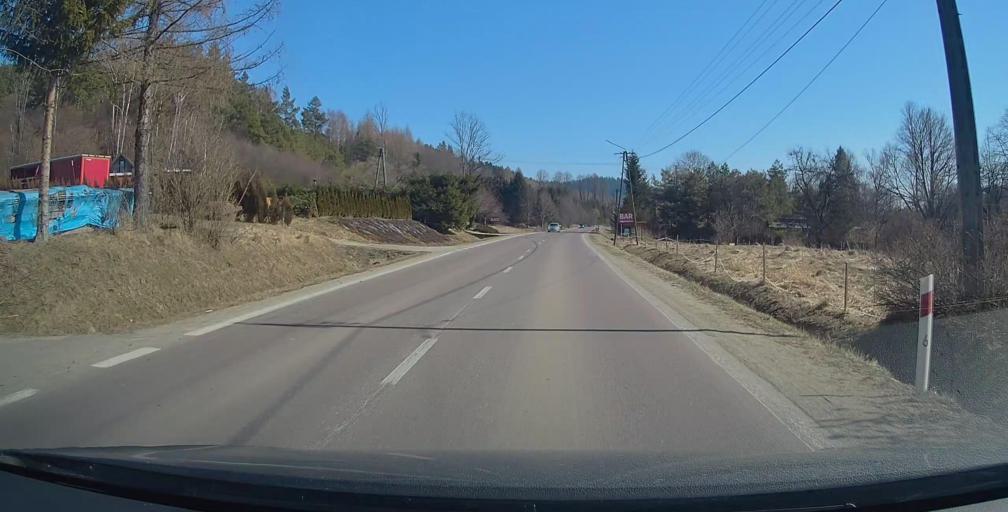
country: PL
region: Subcarpathian Voivodeship
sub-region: Powiat przemyski
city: Bircza
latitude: 49.5761
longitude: 22.5470
